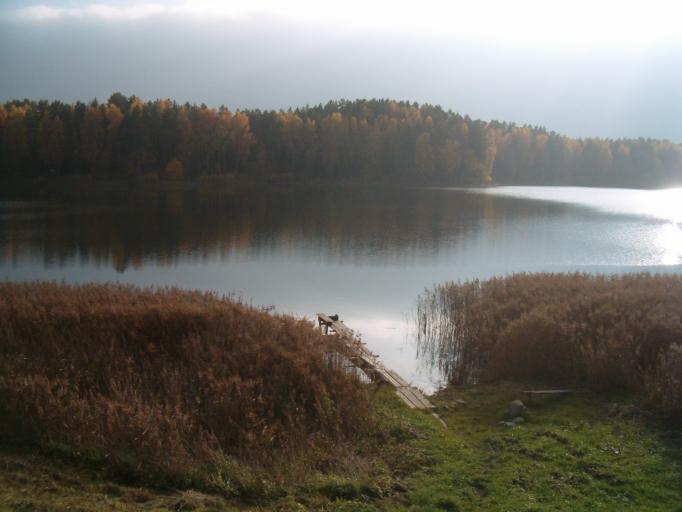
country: LT
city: Zarasai
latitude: 55.6577
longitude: 26.0557
